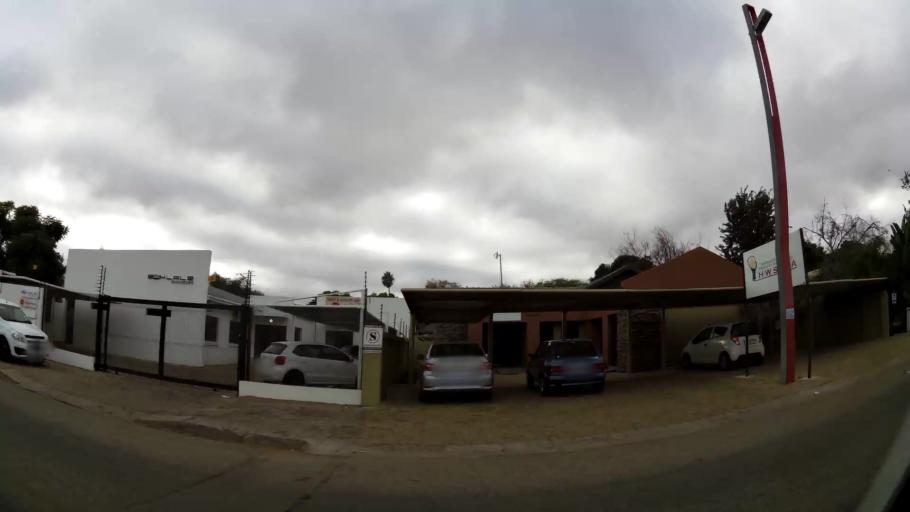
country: ZA
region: Limpopo
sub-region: Capricorn District Municipality
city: Polokwane
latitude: -23.9196
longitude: 29.4550
